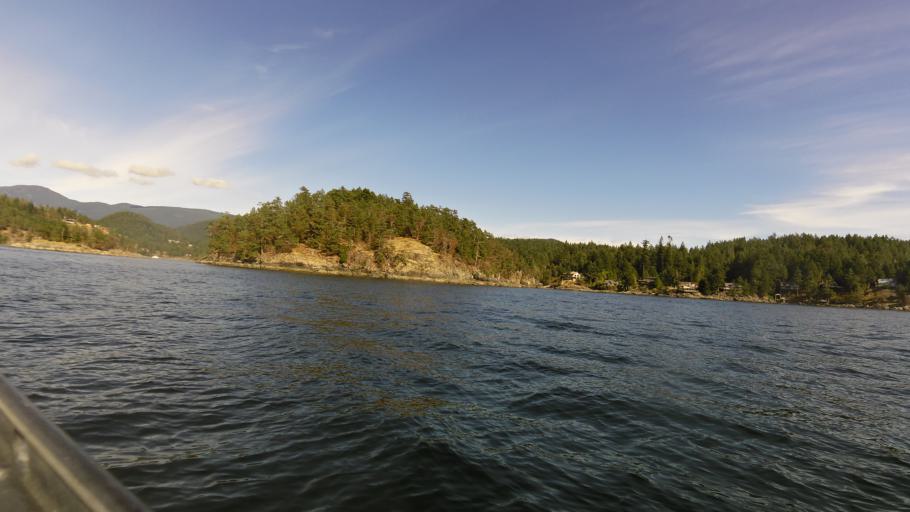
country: CA
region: British Columbia
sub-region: Sunshine Coast Regional District
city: Sechelt
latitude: 49.6266
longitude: -124.0621
